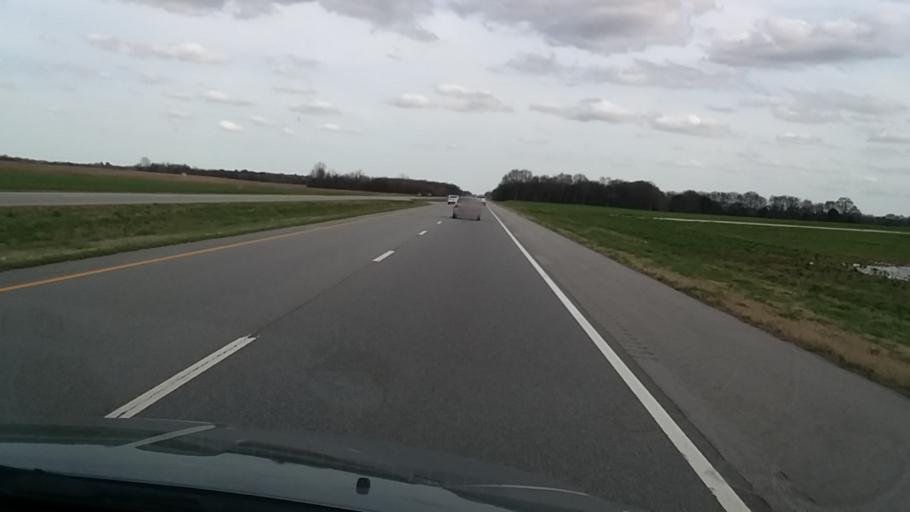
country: US
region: Alabama
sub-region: Lawrence County
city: Town Creek
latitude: 34.6832
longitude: -87.5001
